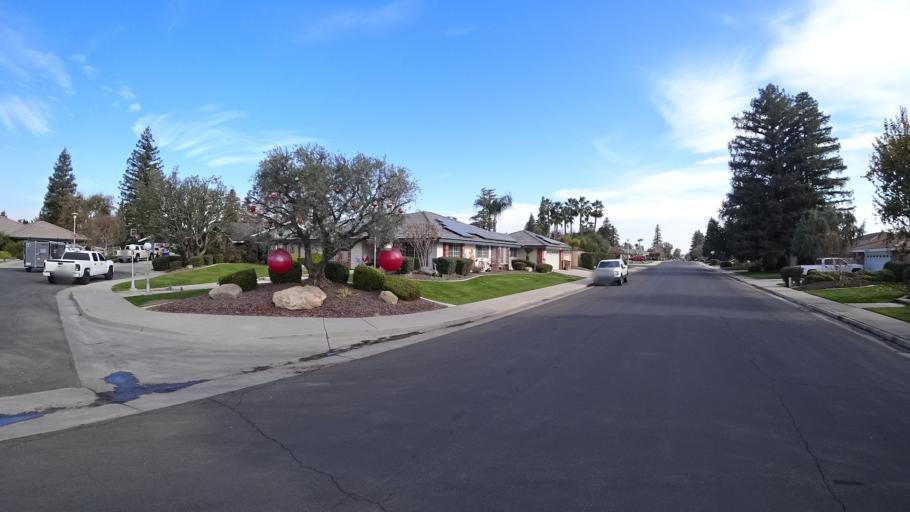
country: US
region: California
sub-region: Kern County
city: Greenacres
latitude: 35.4056
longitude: -119.0811
